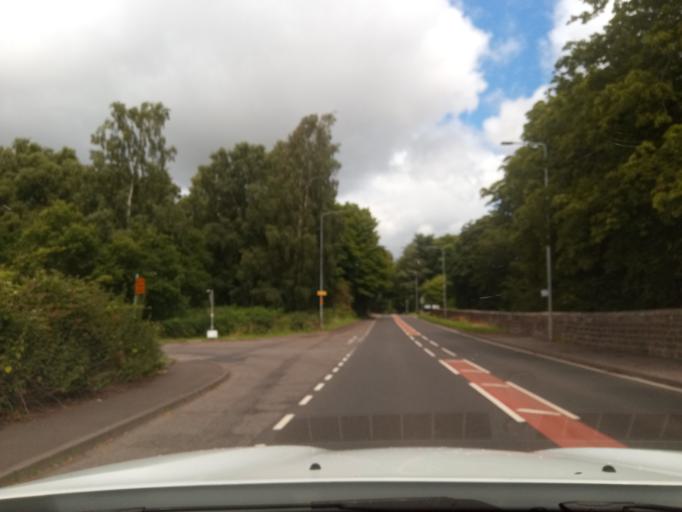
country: GB
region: Scotland
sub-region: Fife
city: Kincardine
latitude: 56.0757
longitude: -3.7207
